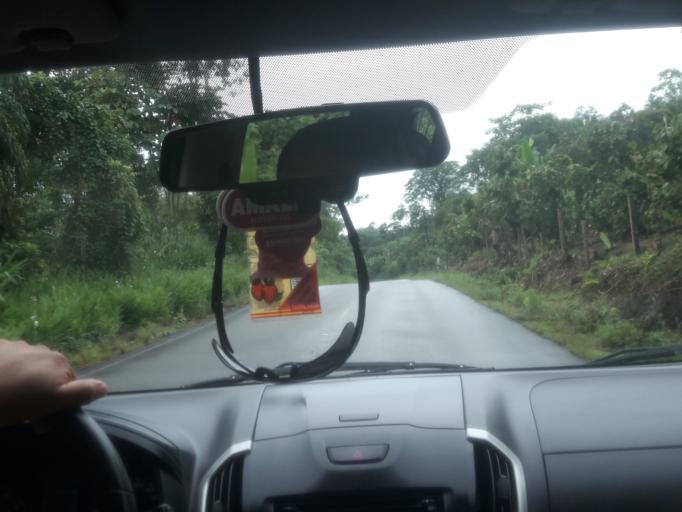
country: EC
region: Napo
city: Tena
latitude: -1.0344
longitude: -77.7212
